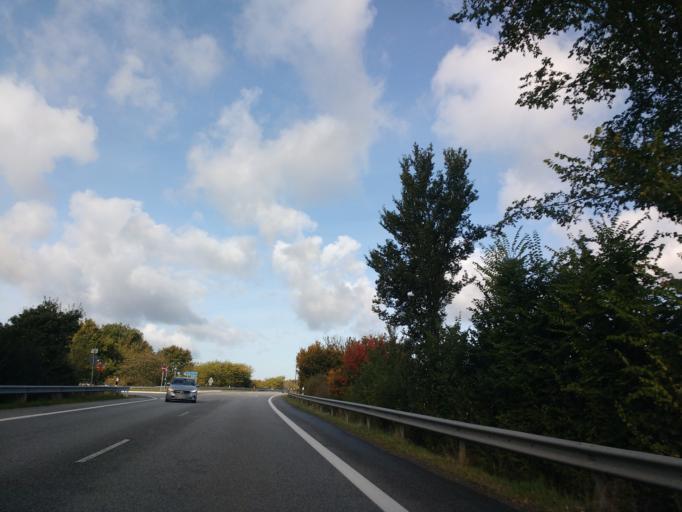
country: DE
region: Schleswig-Holstein
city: Altenkrempe
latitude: 54.1259
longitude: 10.8275
